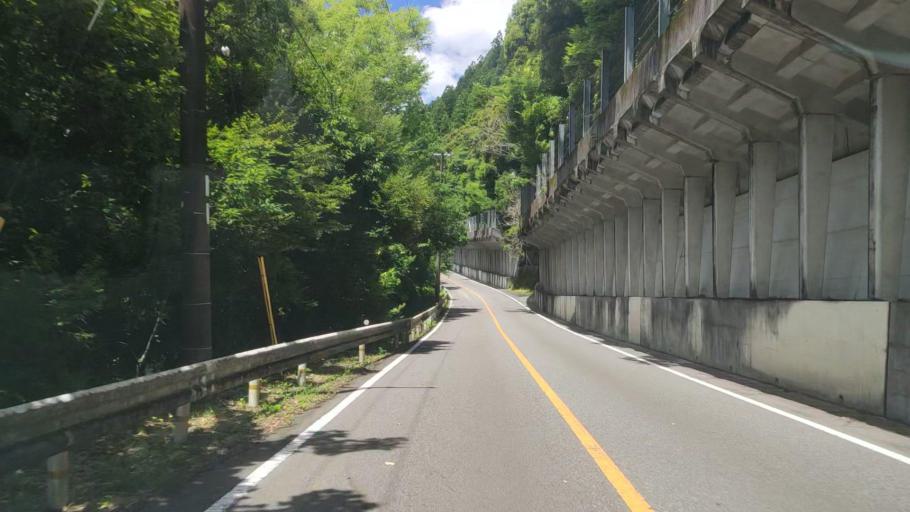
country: JP
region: Mie
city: Owase
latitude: 33.9988
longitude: 136.0112
